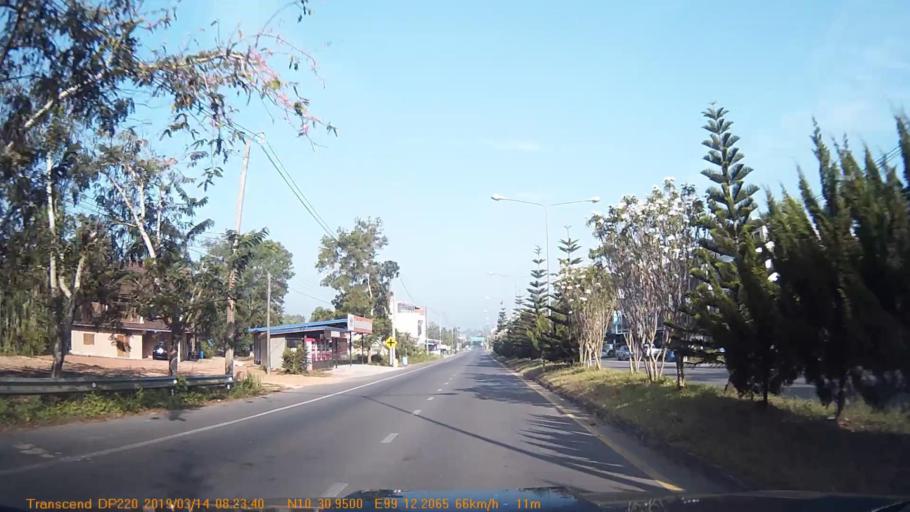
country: TH
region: Chumphon
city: Chumphon
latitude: 10.5159
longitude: 99.2033
